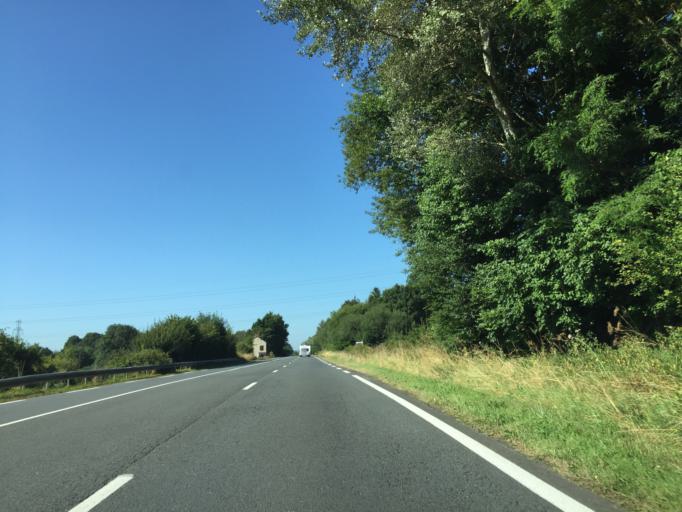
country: FR
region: Lower Normandy
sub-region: Departement du Calvados
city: Lisieux
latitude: 49.2056
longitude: 0.2267
